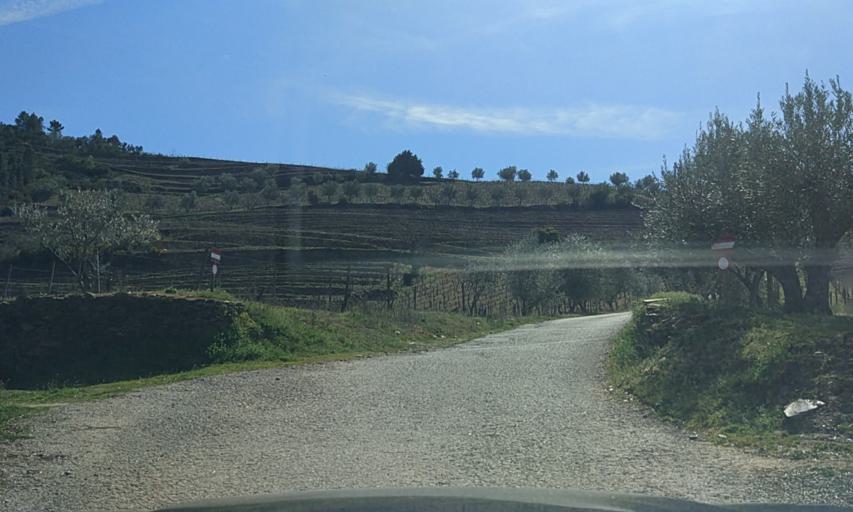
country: PT
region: Vila Real
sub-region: Sabrosa
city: Sabrosa
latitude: 41.3054
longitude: -7.5461
